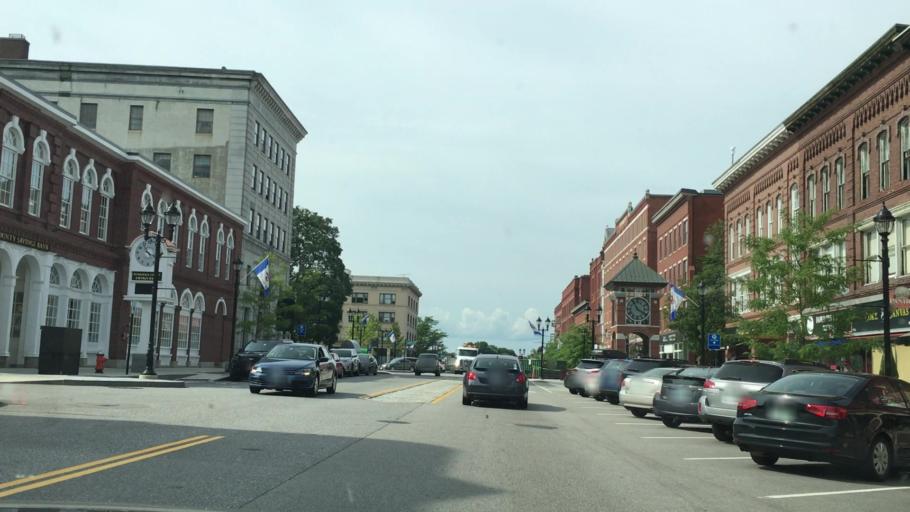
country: US
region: New Hampshire
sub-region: Merrimack County
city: Concord
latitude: 43.2062
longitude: -71.5363
